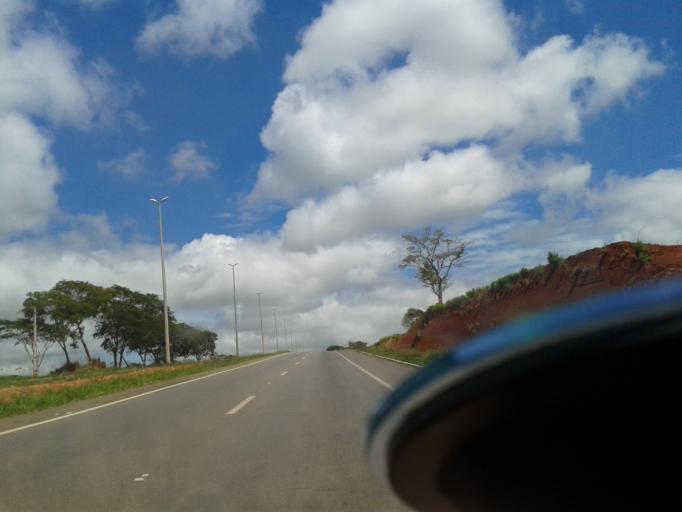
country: BR
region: Goias
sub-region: Inhumas
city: Inhumas
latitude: -16.4134
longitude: -49.4737
